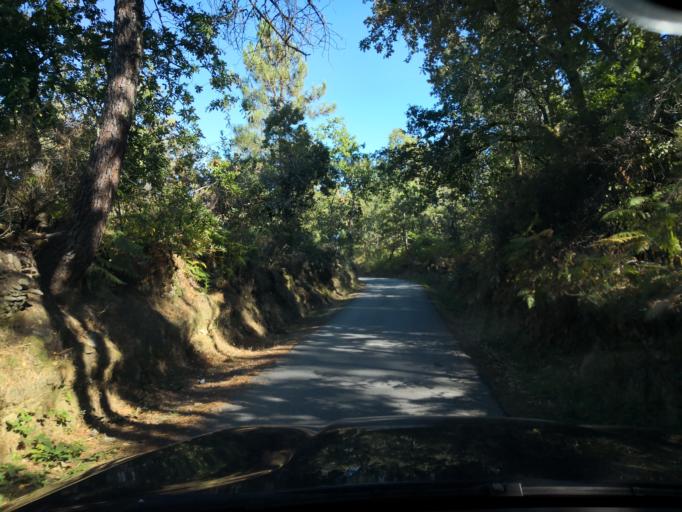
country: PT
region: Vila Real
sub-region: Santa Marta de Penaguiao
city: Santa Marta de Penaguiao
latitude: 41.2856
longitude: -7.8728
